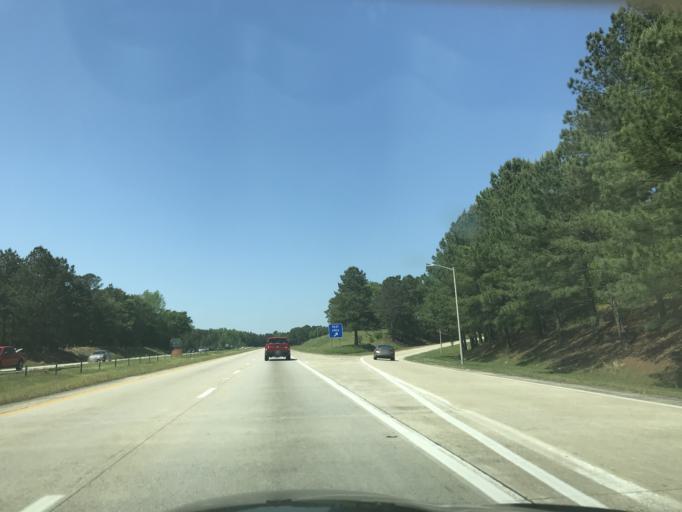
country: US
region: North Carolina
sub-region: Johnston County
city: Benson
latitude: 35.4347
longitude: -78.5330
